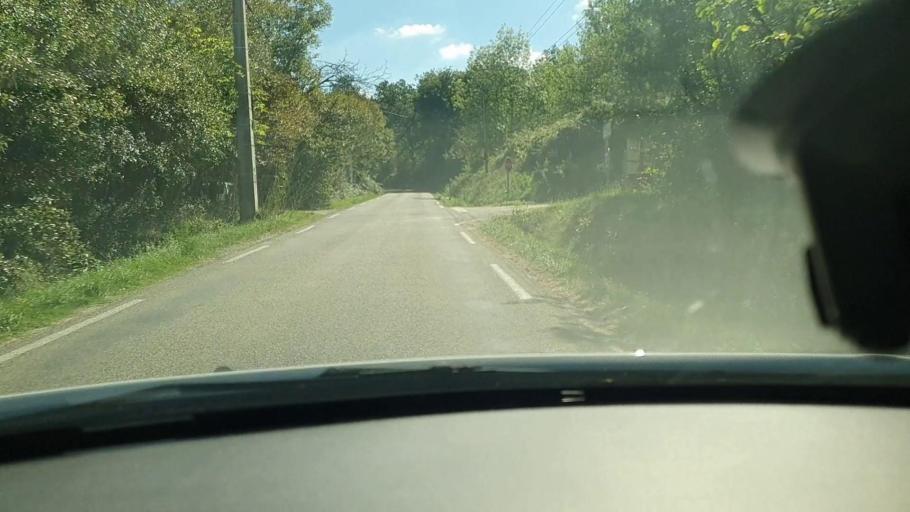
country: FR
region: Languedoc-Roussillon
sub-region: Departement du Gard
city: Goudargues
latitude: 44.1795
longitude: 4.4781
